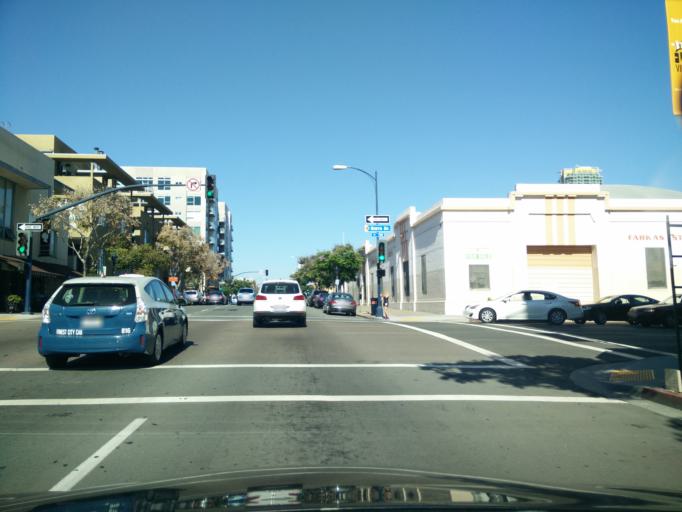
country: US
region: California
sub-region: San Diego County
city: San Diego
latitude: 32.7126
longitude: -117.1567
